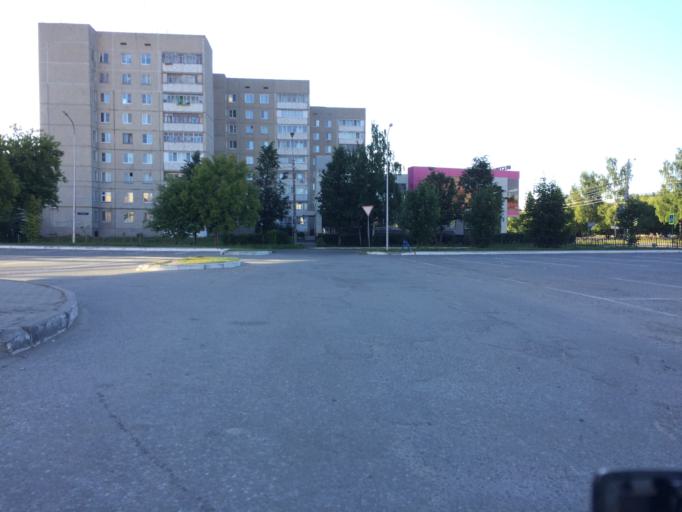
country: RU
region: Mariy-El
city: Medvedevo
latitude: 56.6416
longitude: 47.8345
